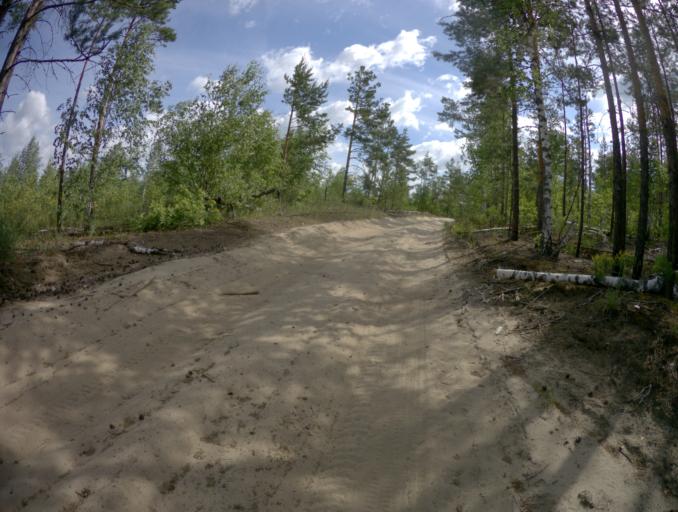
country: RU
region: Ivanovo
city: Talitsy
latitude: 56.5339
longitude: 42.4203
